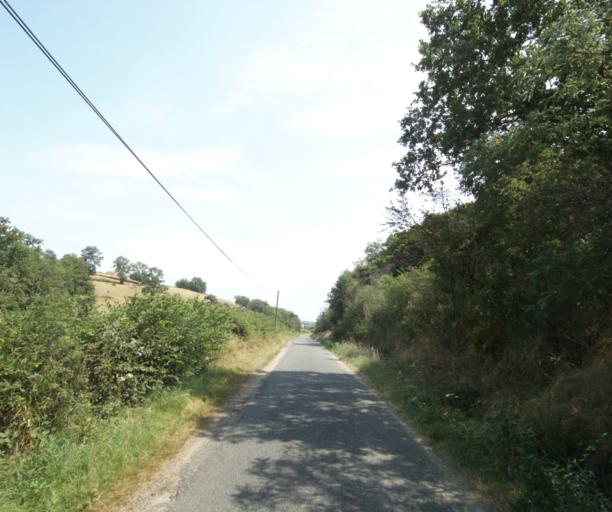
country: FR
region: Bourgogne
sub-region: Departement de Saone-et-Loire
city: Gueugnon
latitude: 46.6191
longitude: 4.0260
